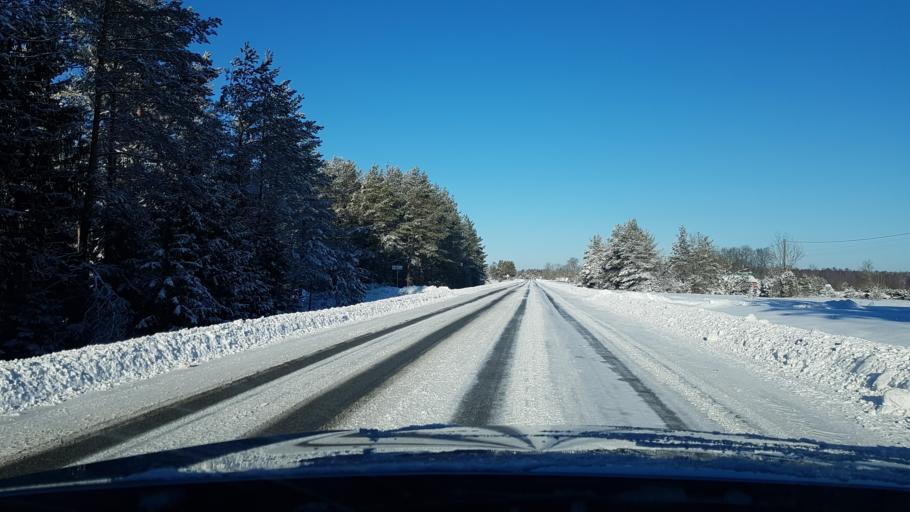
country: EE
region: Hiiumaa
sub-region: Kaerdla linn
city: Kardla
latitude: 58.9507
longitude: 22.7720
